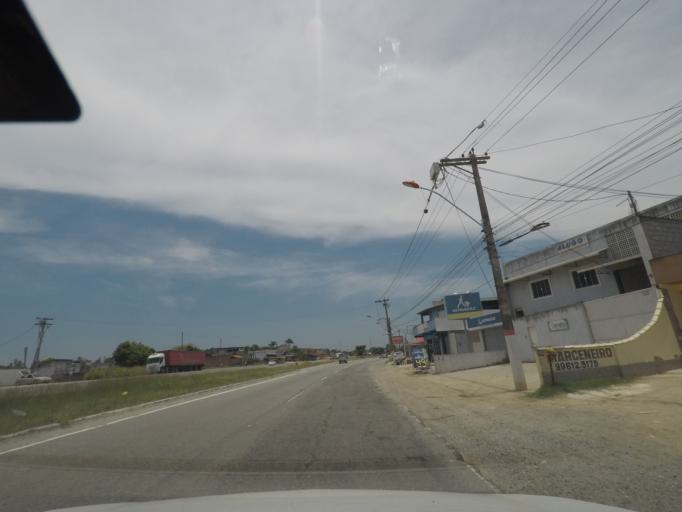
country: BR
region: Rio de Janeiro
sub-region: Marica
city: Marica
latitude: -22.9301
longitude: -42.8727
